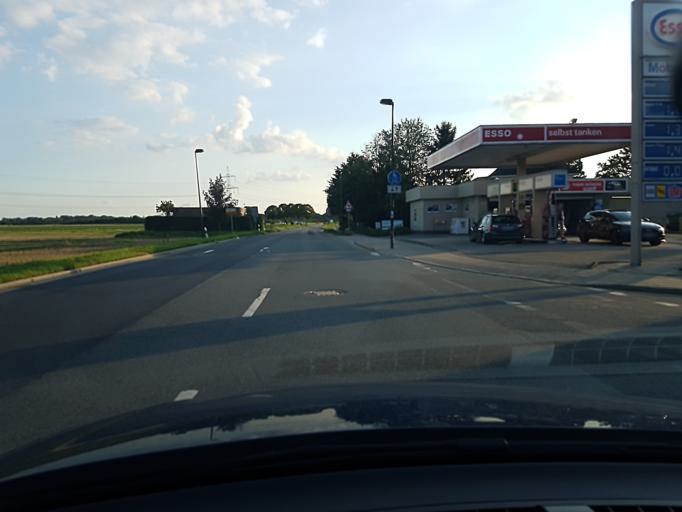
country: DE
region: North Rhine-Westphalia
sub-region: Regierungsbezirk Dusseldorf
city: Ratingen
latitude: 51.3233
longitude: 6.7707
